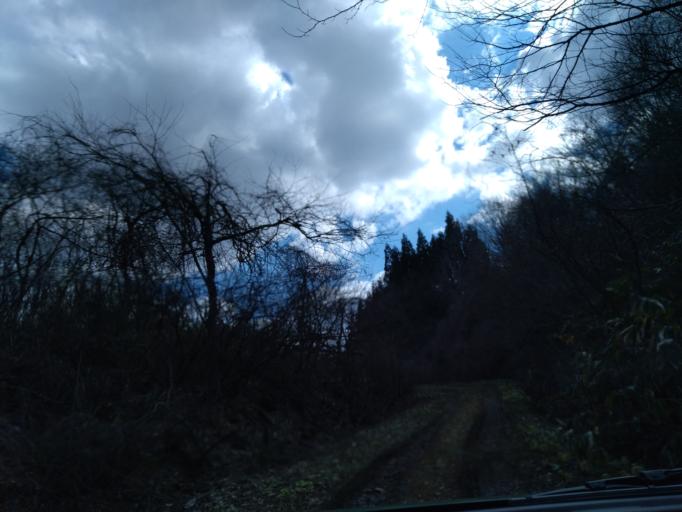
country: JP
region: Iwate
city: Ichinoseki
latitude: 38.9824
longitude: 141.0188
